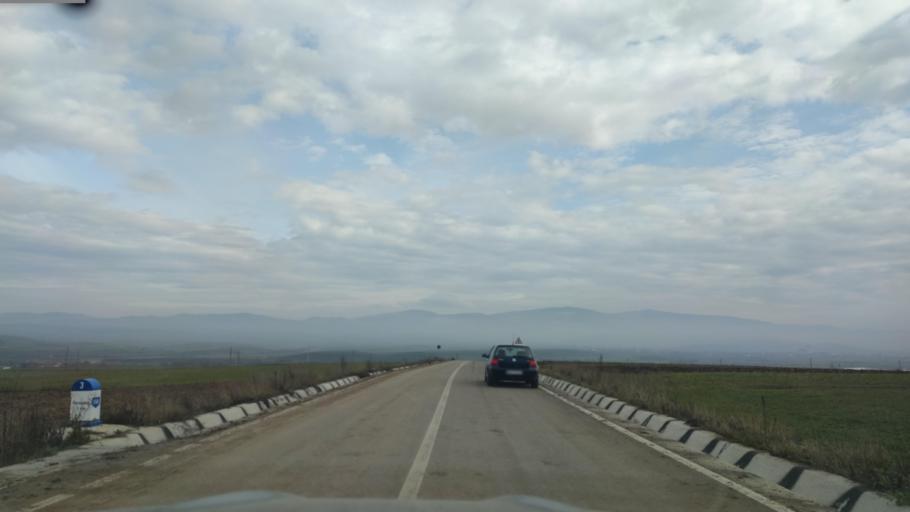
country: RO
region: Harghita
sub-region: Comuna Subcetate
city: Subcetate
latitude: 46.8179
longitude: 25.4486
